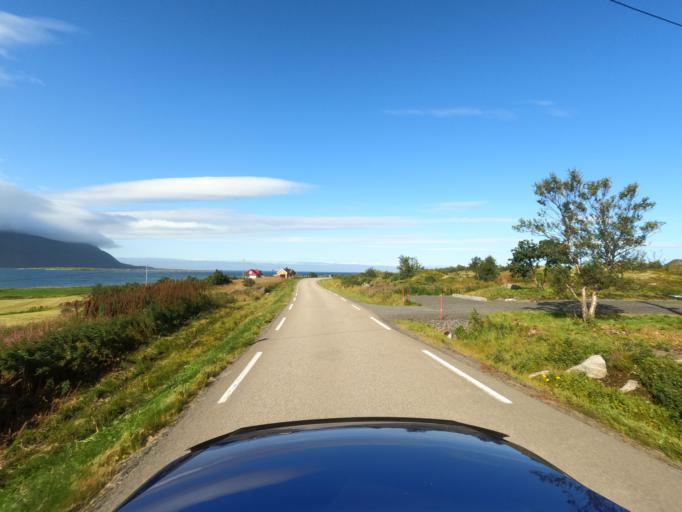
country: NO
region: Nordland
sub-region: Vestvagoy
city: Evjen
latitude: 68.3306
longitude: 14.0914
